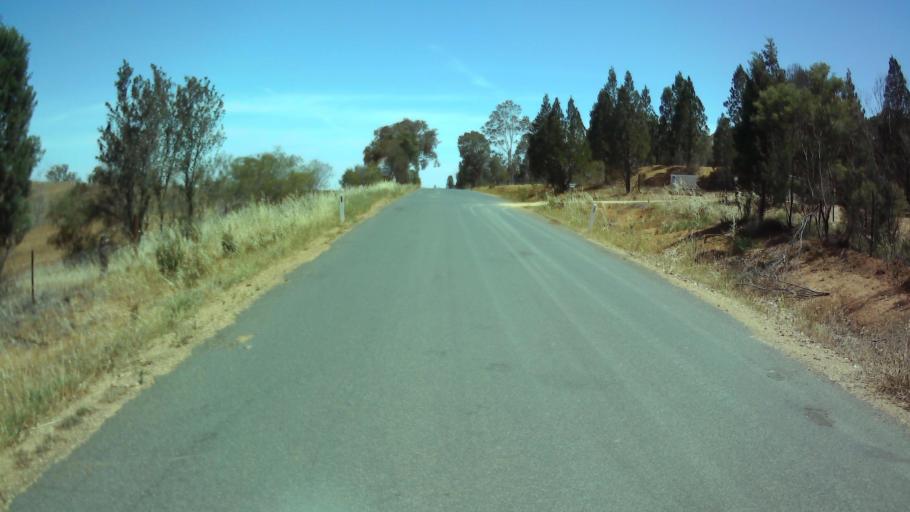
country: AU
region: New South Wales
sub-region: Weddin
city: Grenfell
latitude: -33.9031
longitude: 148.1834
